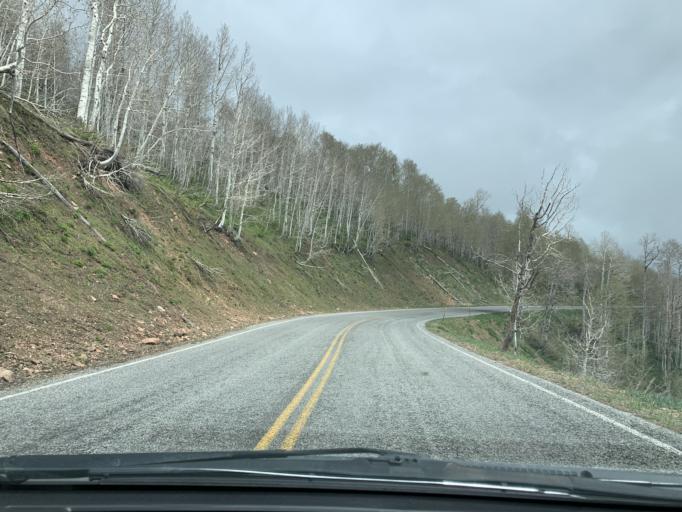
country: US
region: Utah
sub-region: Utah County
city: Elk Ridge
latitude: 39.8741
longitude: -111.6841
